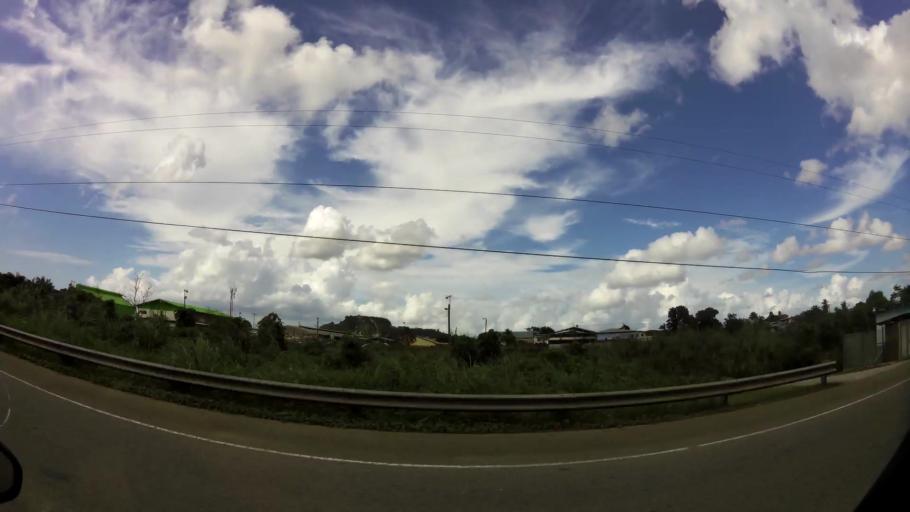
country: TT
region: City of San Fernando
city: Mon Repos
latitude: 10.2611
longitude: -61.4532
